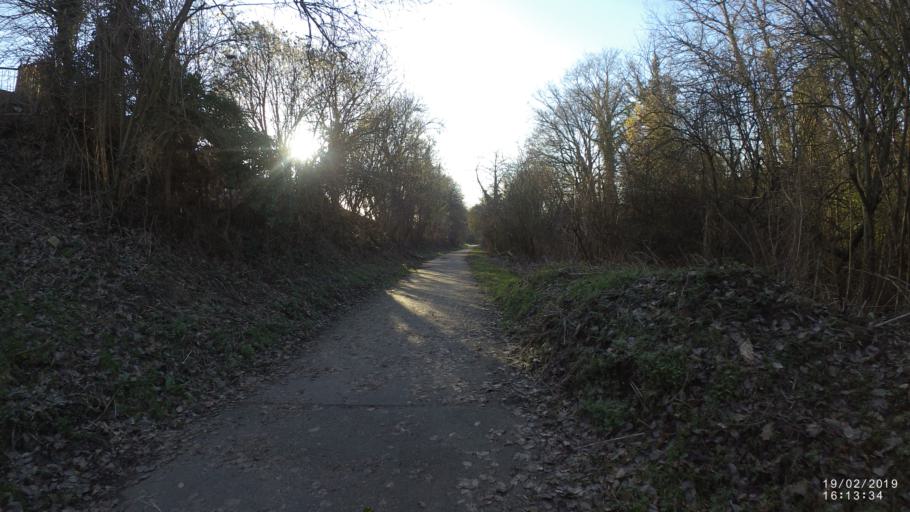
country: BE
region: Flanders
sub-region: Provincie Limburg
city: Borgloon
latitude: 50.8133
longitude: 5.3578
